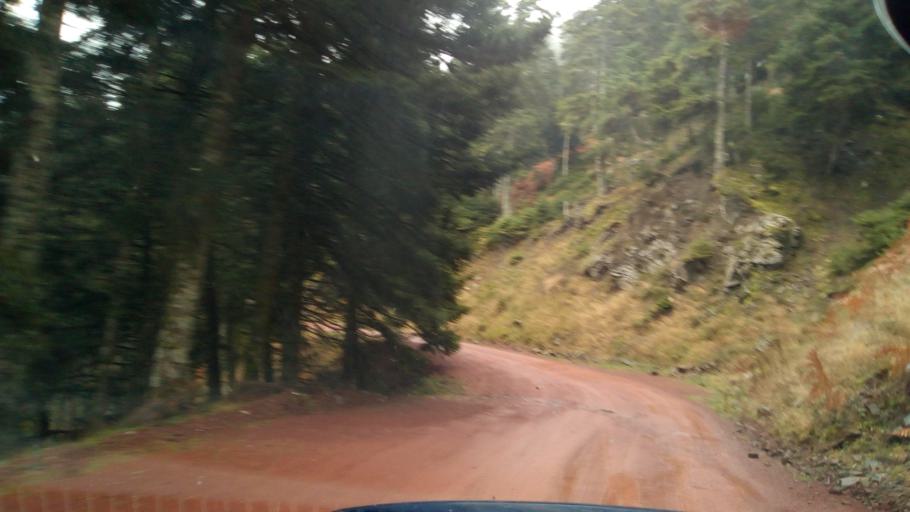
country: GR
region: West Greece
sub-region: Nomos Aitolias kai Akarnanias
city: Nafpaktos
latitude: 38.5417
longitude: 21.8647
